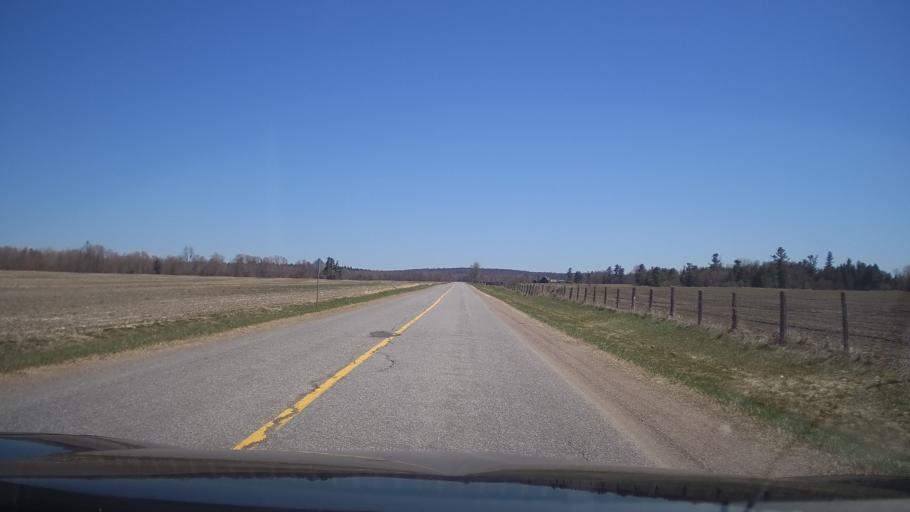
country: CA
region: Quebec
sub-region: Outaouais
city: Shawville
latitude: 45.5385
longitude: -76.3940
